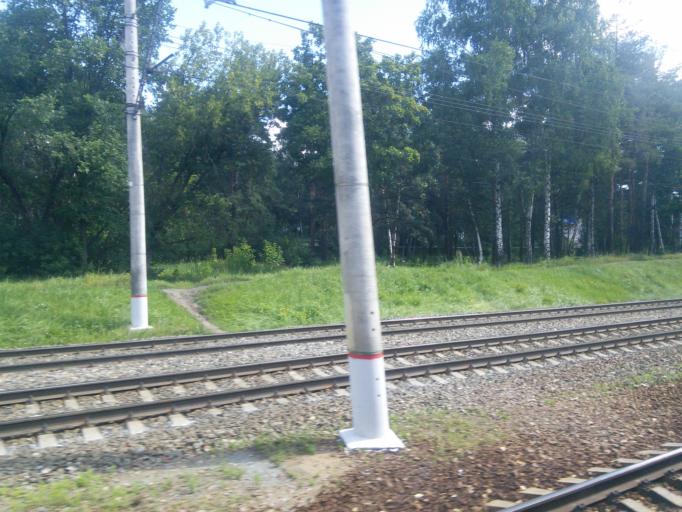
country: RU
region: Moskovskaya
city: Kratovo
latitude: 55.5784
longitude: 38.1933
